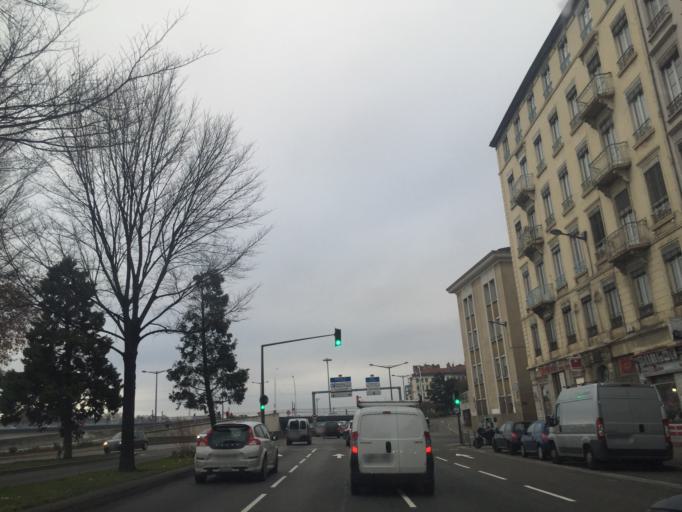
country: FR
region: Rhone-Alpes
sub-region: Departement du Rhone
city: Lyon
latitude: 45.7502
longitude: 4.8317
